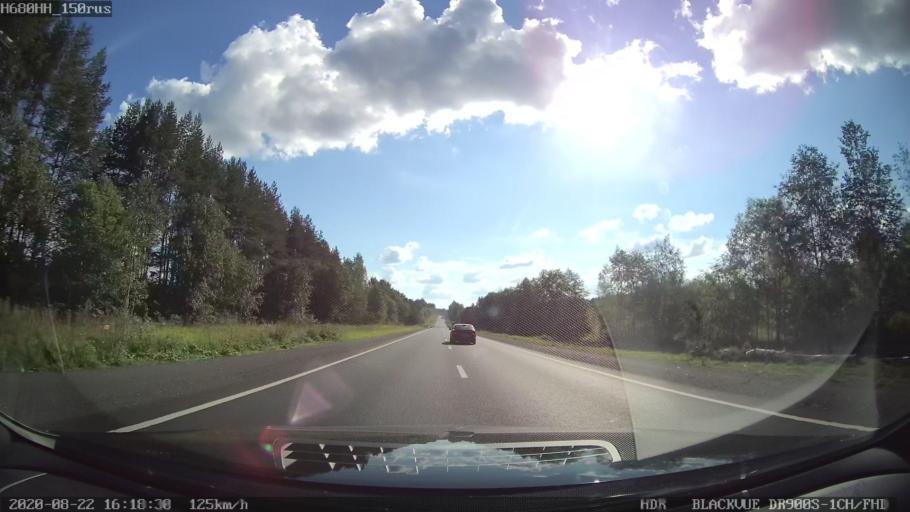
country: RU
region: Tverskaya
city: Rameshki
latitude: 57.4157
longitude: 36.1392
